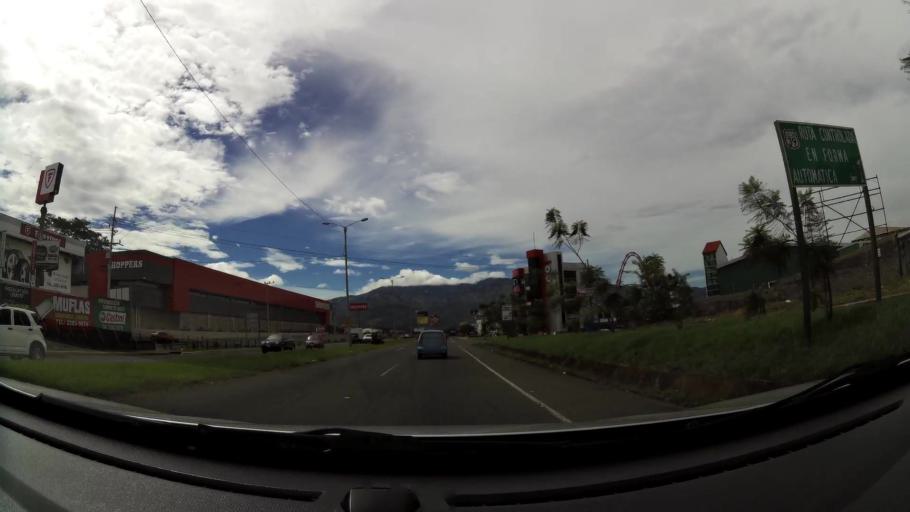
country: CR
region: San Jose
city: San Pedro
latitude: 9.9201
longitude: -84.0611
